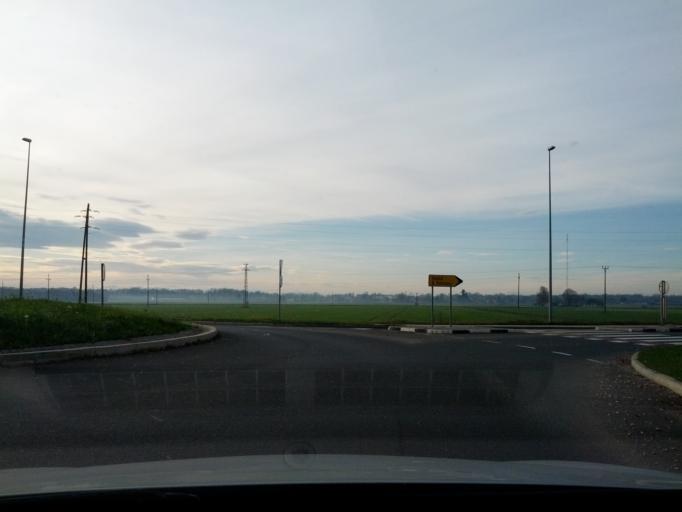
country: SI
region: Murska Sobota
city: Murska Sobota
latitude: 46.6845
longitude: 16.1820
